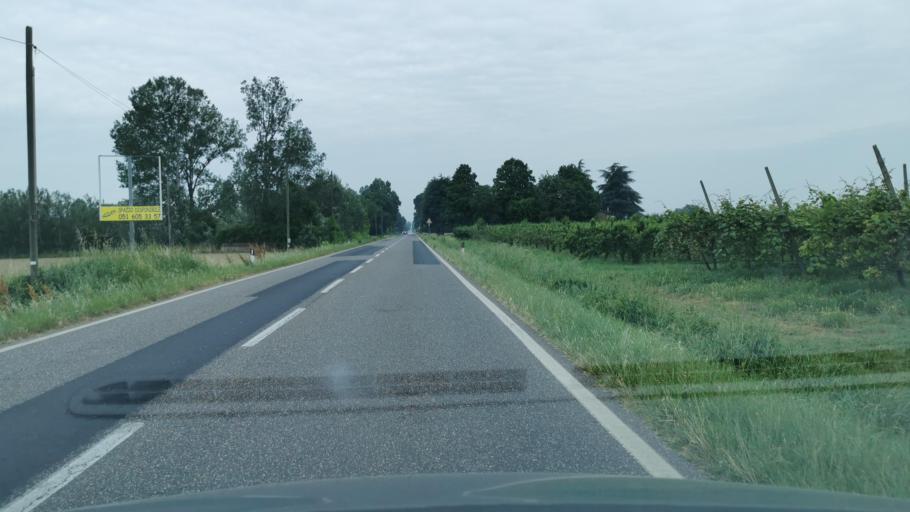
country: IT
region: Emilia-Romagna
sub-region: Provincia di Ravenna
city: Russi
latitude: 44.3930
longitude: 12.0441
